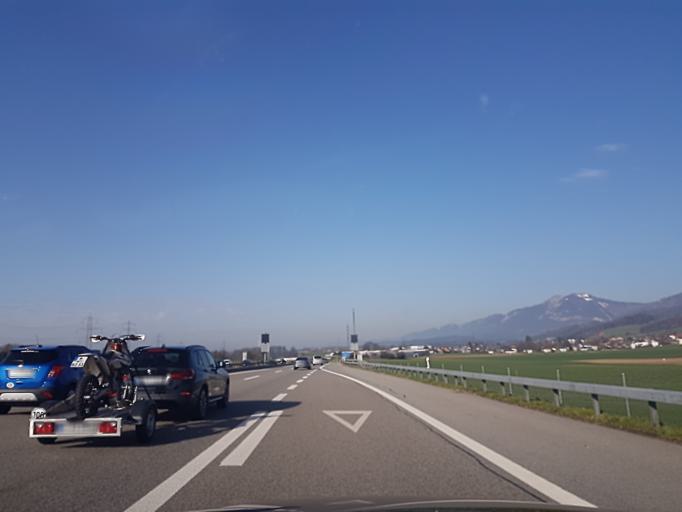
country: CH
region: Bern
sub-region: Oberaargau
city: Oberbipp
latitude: 47.2485
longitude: 7.6652
